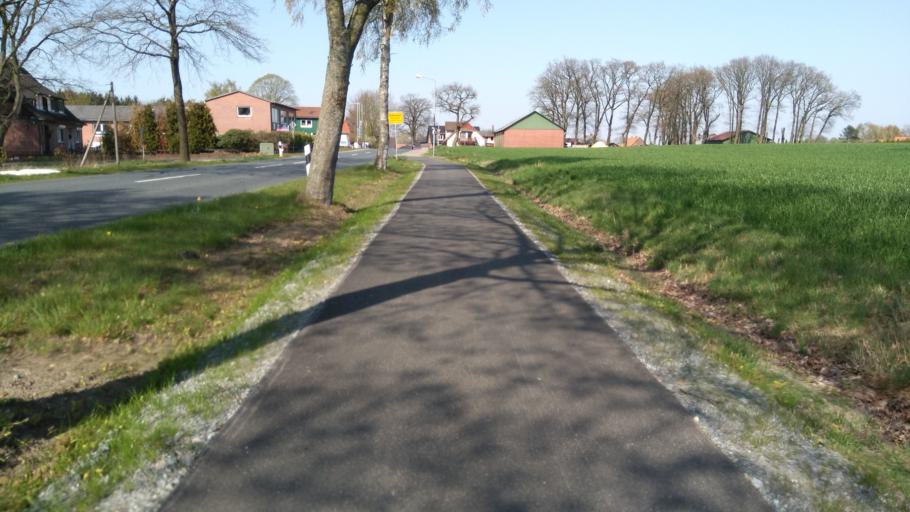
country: DE
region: Lower Saxony
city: Bliedersdorf
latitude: 53.4769
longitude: 9.5654
